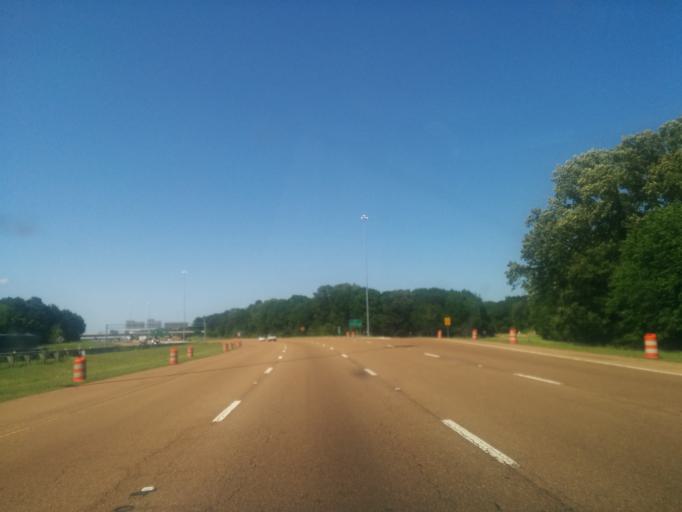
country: US
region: Mississippi
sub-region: Madison County
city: Ridgeland
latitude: 32.4225
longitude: -90.1443
